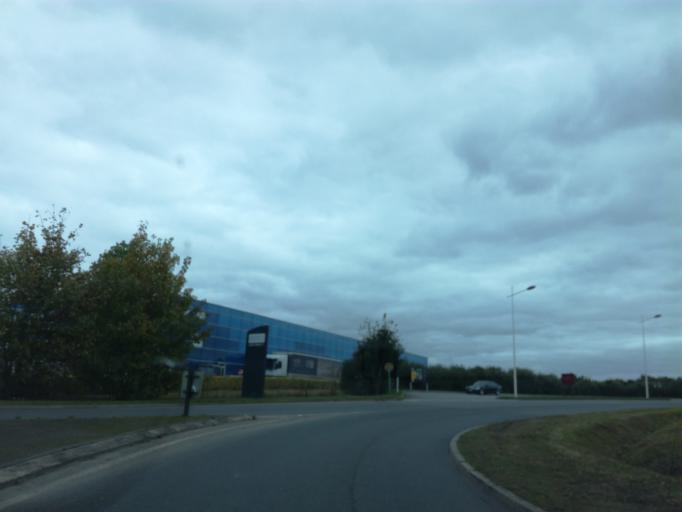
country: FR
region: Brittany
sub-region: Departement des Cotes-d'Armor
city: Loudeac
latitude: 48.1525
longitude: -2.7594
